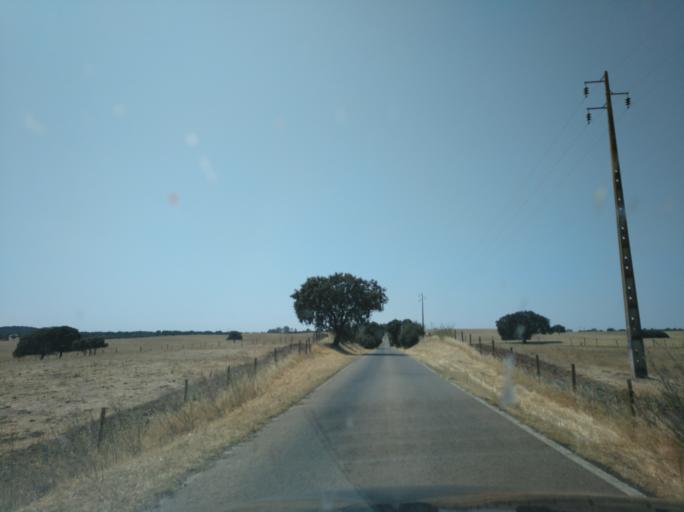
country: PT
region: Portalegre
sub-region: Campo Maior
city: Campo Maior
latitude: 39.0117
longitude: -6.9828
